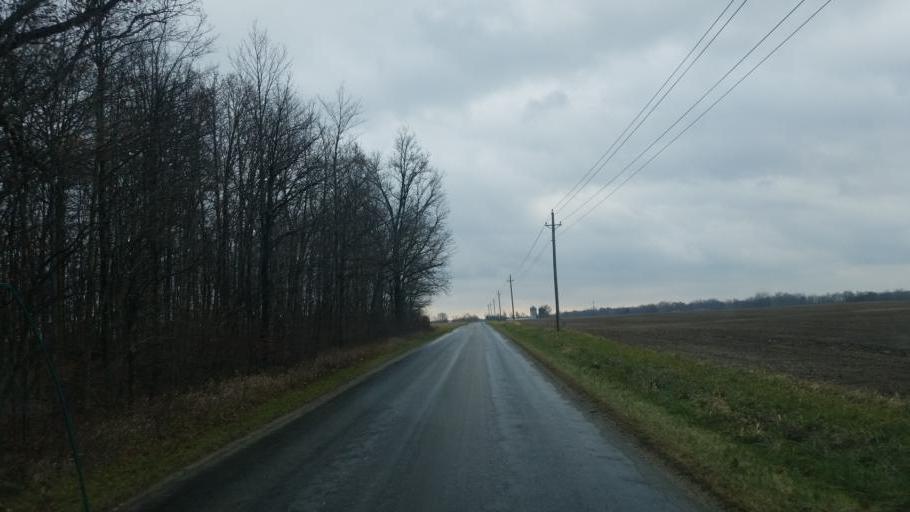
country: US
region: Indiana
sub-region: Adams County
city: Geneva
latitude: 40.5522
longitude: -84.9917
